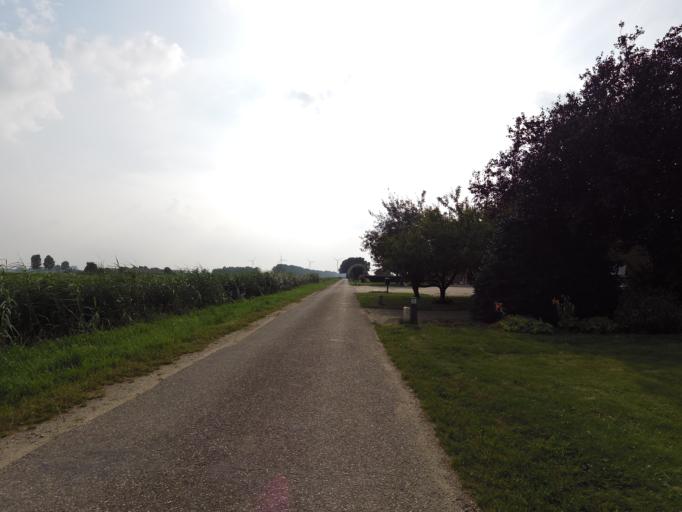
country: NL
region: Gelderland
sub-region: Gemeente Rheden
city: Rheden
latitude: 51.9811
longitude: 6.0512
